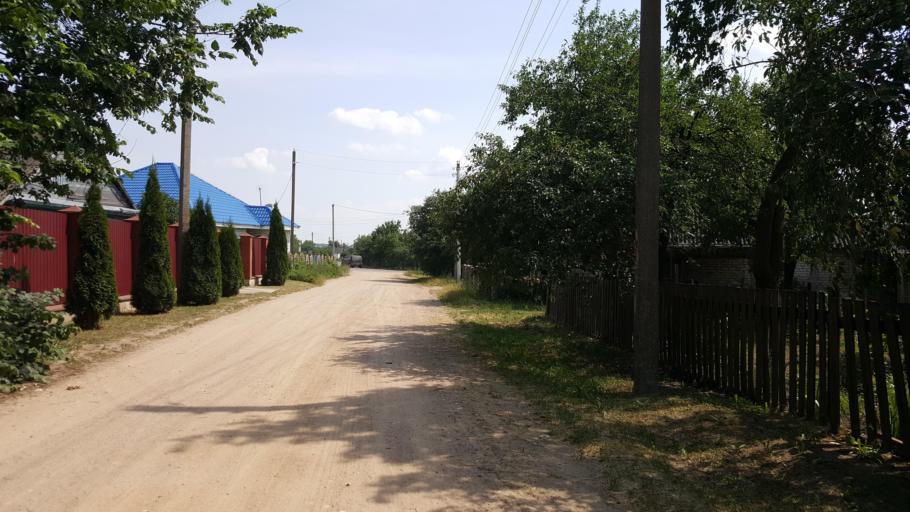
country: BY
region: Brest
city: Kamyanyets
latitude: 52.3299
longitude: 23.7779
